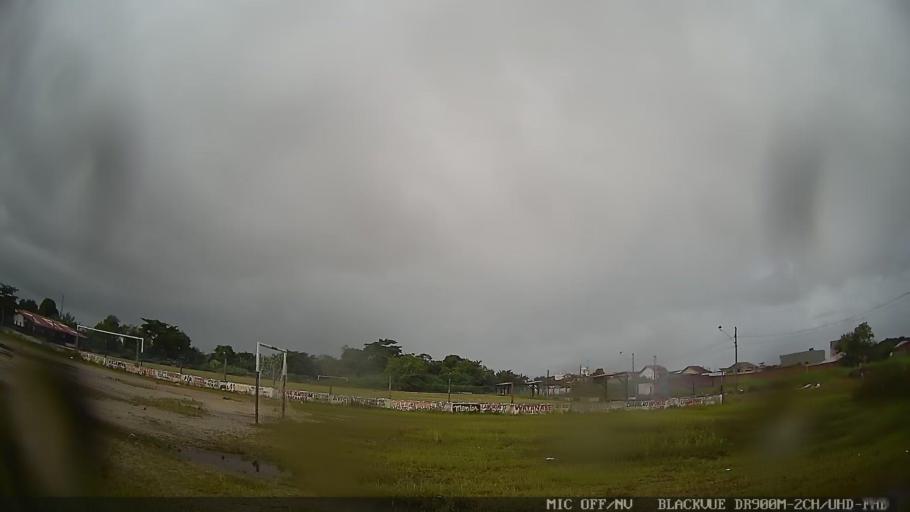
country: BR
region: Sao Paulo
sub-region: Itanhaem
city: Itanhaem
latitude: -24.1916
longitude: -46.8233
